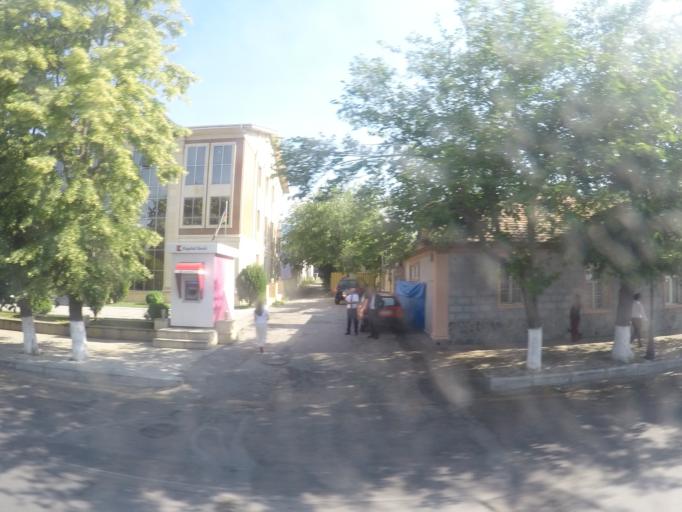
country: AZ
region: Shaki City
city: Sheki
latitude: 41.2013
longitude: 47.1749
